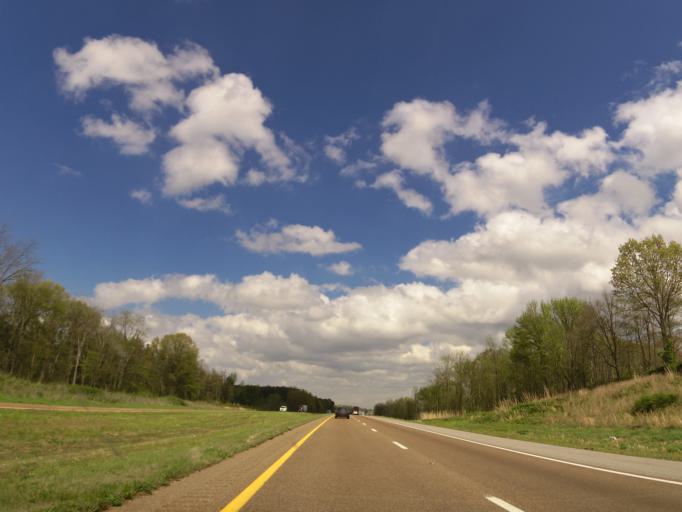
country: US
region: Tennessee
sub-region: Tipton County
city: Mason
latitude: 35.3327
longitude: -89.5529
